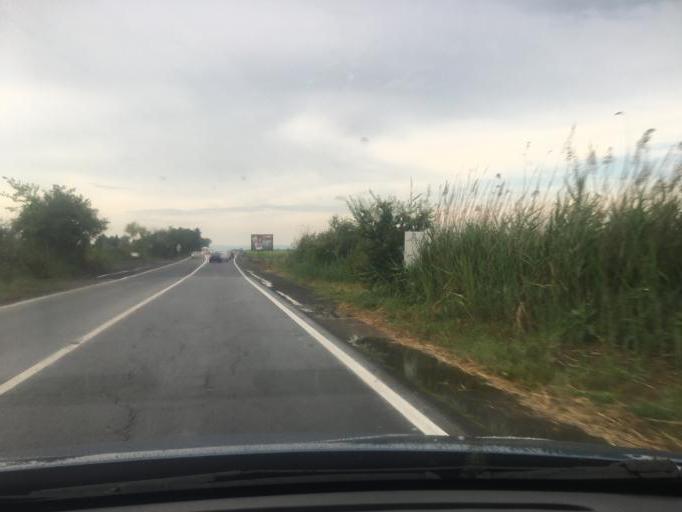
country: BG
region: Burgas
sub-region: Obshtina Pomorie
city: Pomorie
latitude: 42.5935
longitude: 27.6138
